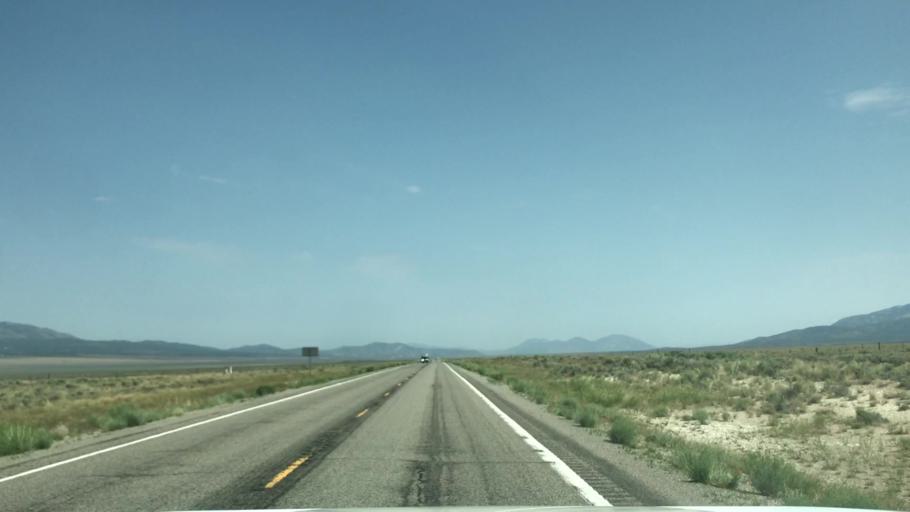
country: US
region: Nevada
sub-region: White Pine County
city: Ely
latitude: 39.0679
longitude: -114.7372
